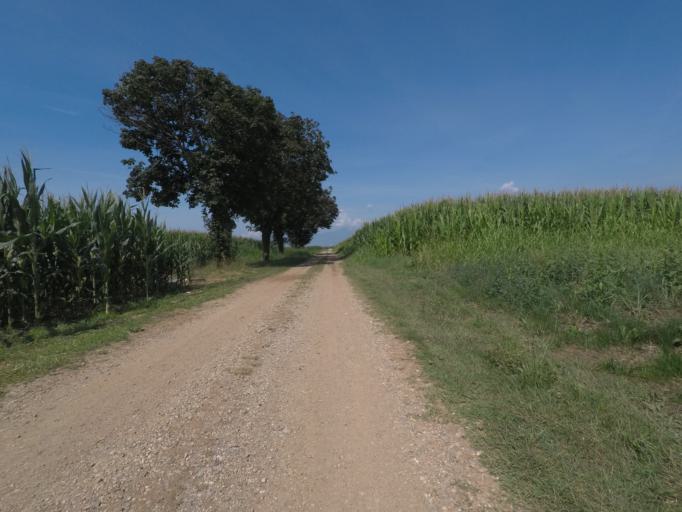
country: IT
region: Friuli Venezia Giulia
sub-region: Provincia di Udine
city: Dignano
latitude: 46.0826
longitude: 12.9681
